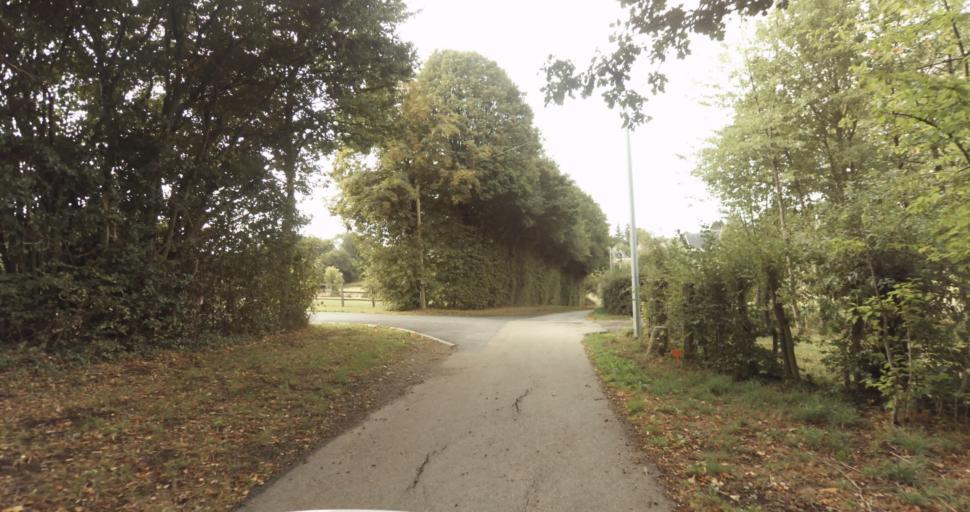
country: FR
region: Lower Normandy
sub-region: Departement de l'Orne
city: Gace
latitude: 48.8332
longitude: 0.3821
